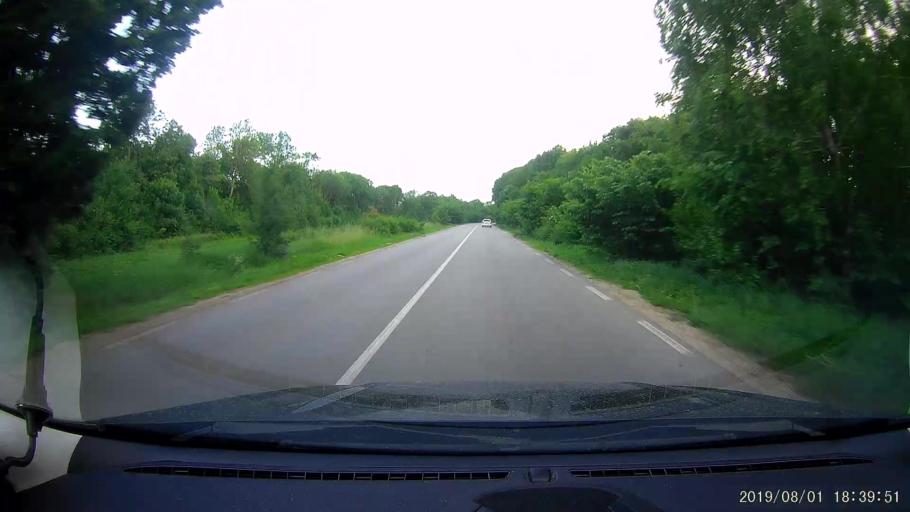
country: BG
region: Shumen
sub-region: Obshtina Khitrino
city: Gara Khitrino
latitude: 43.3771
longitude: 26.9189
